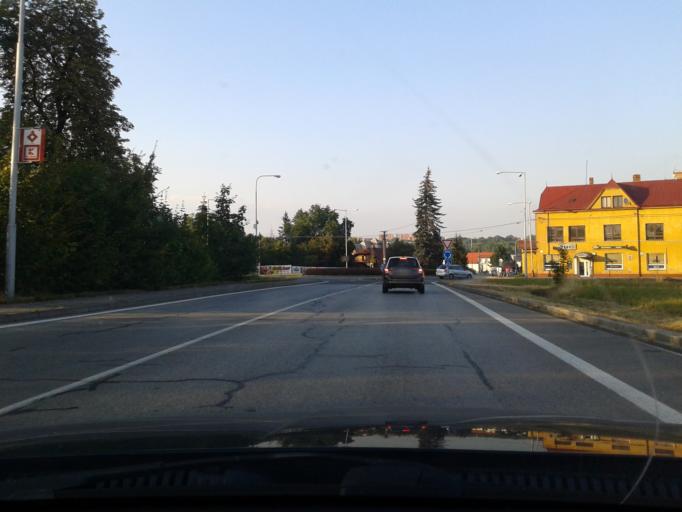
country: CZ
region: Moravskoslezsky
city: Orlova
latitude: 49.8481
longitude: 18.4154
